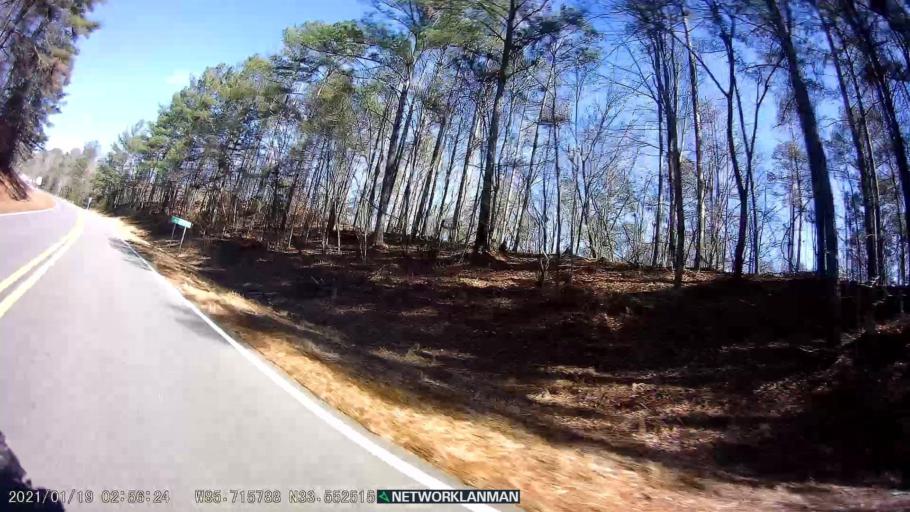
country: US
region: Alabama
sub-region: Calhoun County
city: Choccolocco
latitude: 33.5526
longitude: -85.7157
